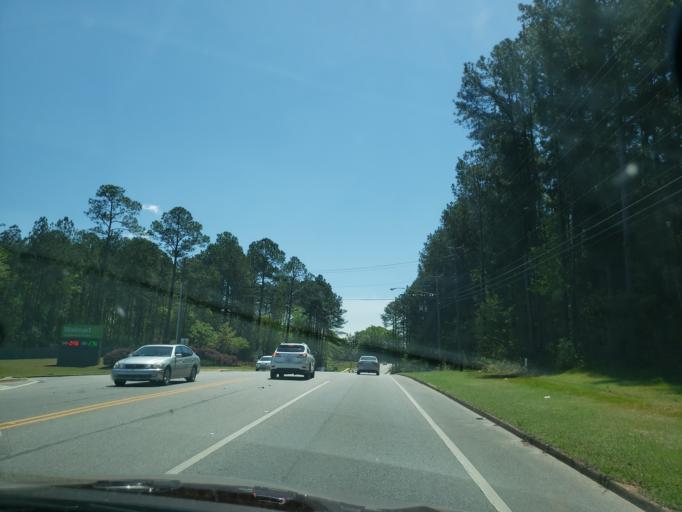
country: US
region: Alabama
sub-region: Lee County
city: Auburn
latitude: 32.6293
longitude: -85.4966
